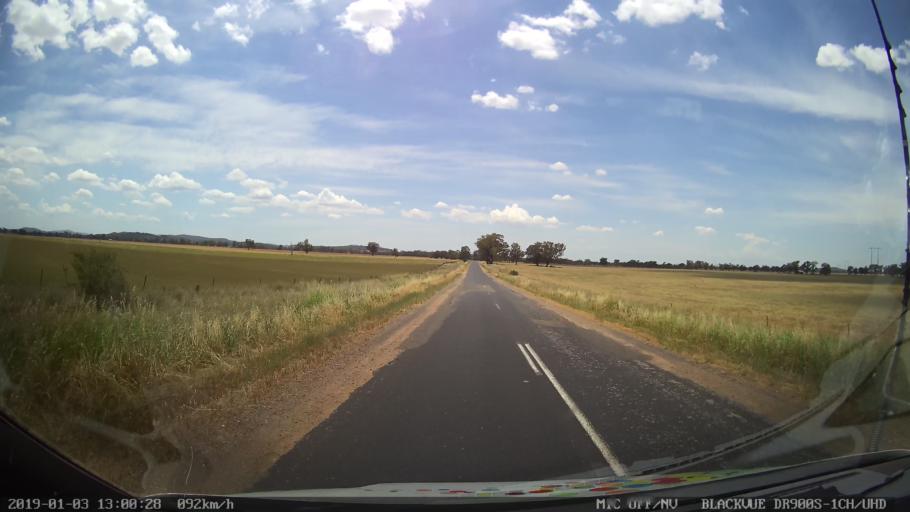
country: AU
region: New South Wales
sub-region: Cabonne
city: Canowindra
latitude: -33.6308
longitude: 148.4041
